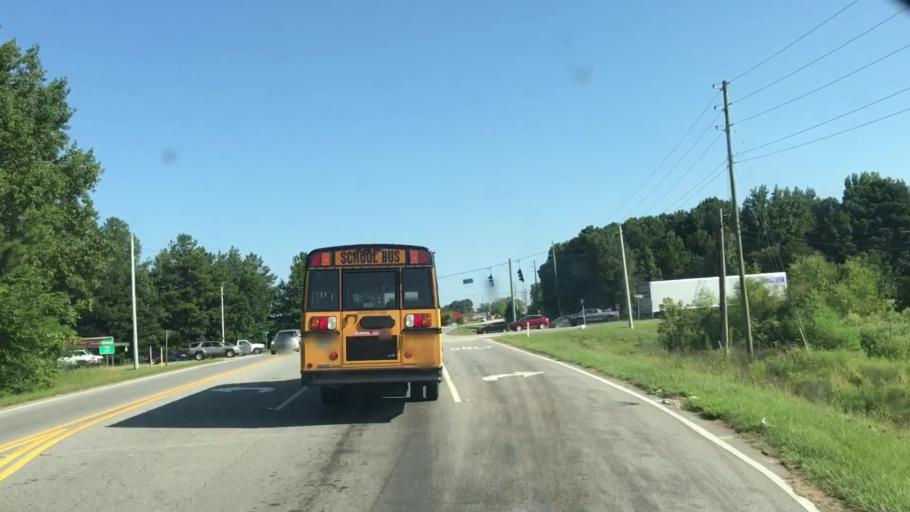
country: US
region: Georgia
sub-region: Gwinnett County
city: Lawrenceville
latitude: 33.9808
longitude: -83.9725
